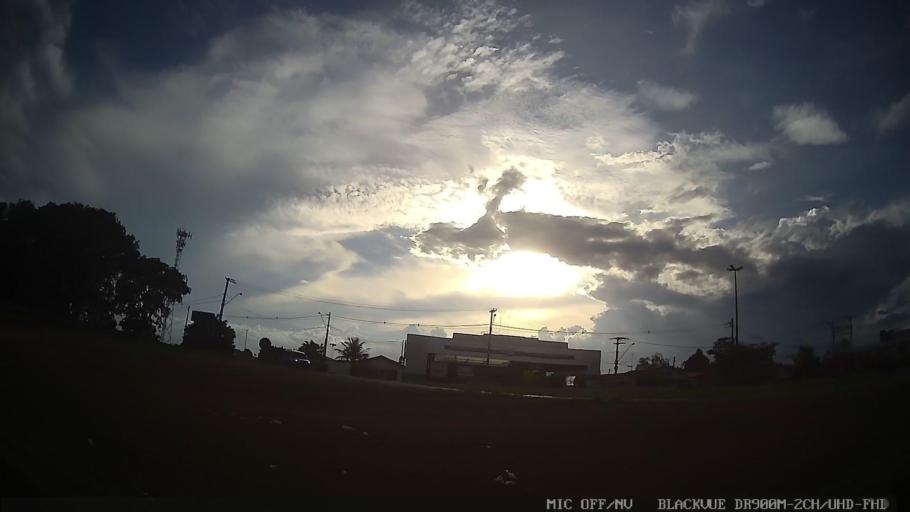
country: BR
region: Sao Paulo
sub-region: Tiete
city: Tiete
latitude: -23.0856
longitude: -47.7189
